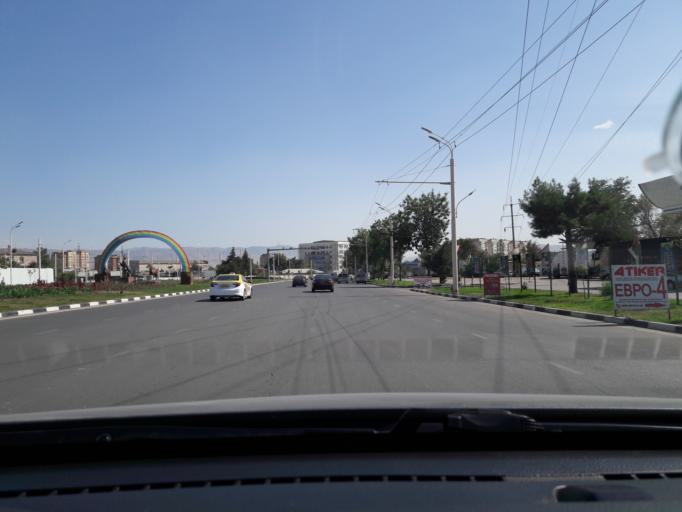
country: TJ
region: Dushanbe
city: Dushanbe
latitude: 38.5387
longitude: 68.7409
